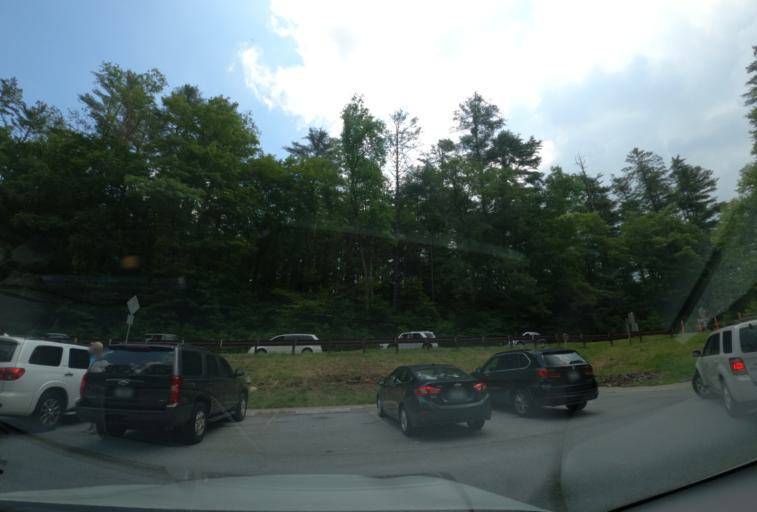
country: US
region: North Carolina
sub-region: Macon County
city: Franklin
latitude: 35.0681
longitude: -83.2385
